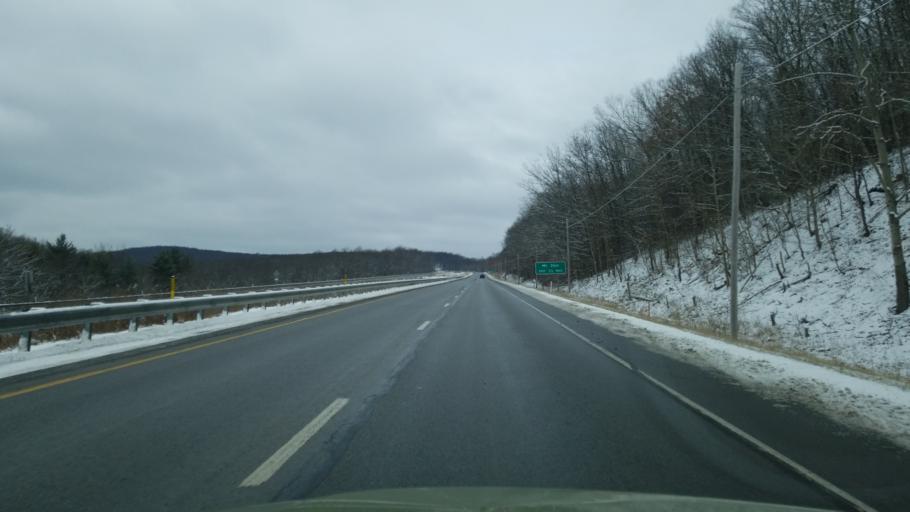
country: US
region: Pennsylvania
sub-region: Clearfield County
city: Clearfield
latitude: 41.0528
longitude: -78.4775
